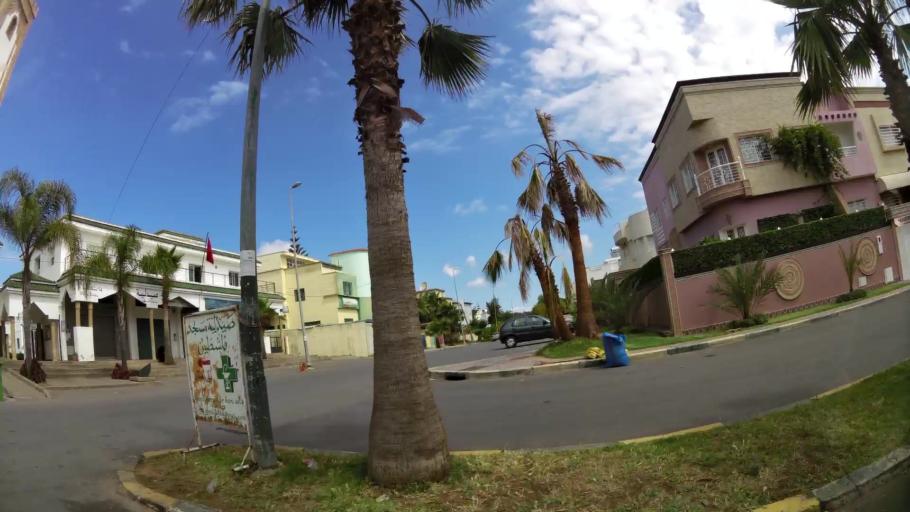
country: MA
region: Gharb-Chrarda-Beni Hssen
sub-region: Kenitra Province
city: Kenitra
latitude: 34.2427
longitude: -6.6050
